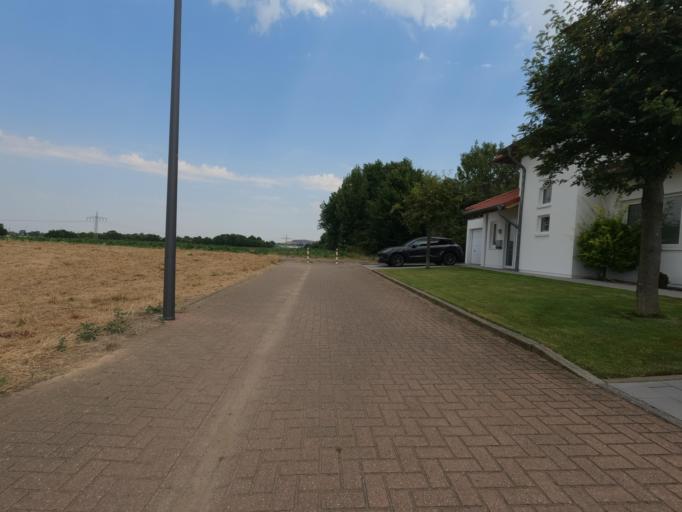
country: DE
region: North Rhine-Westphalia
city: Baesweiler
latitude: 50.9158
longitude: 6.1863
